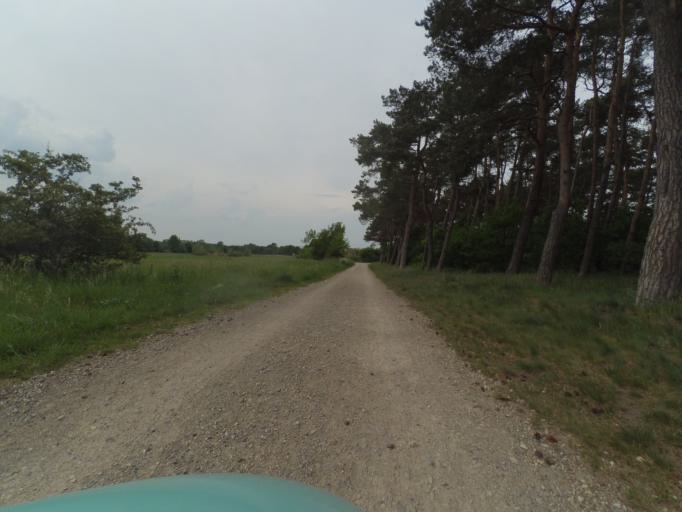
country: DE
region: Lower Saxony
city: Burgdorf
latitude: 52.4323
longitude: 10.0041
